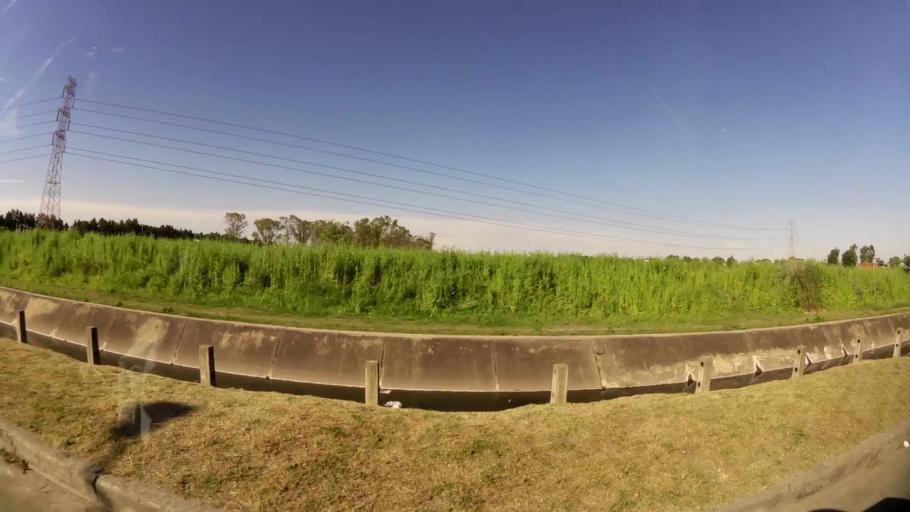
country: AR
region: Buenos Aires
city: Hurlingham
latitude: -34.5514
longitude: -58.6070
